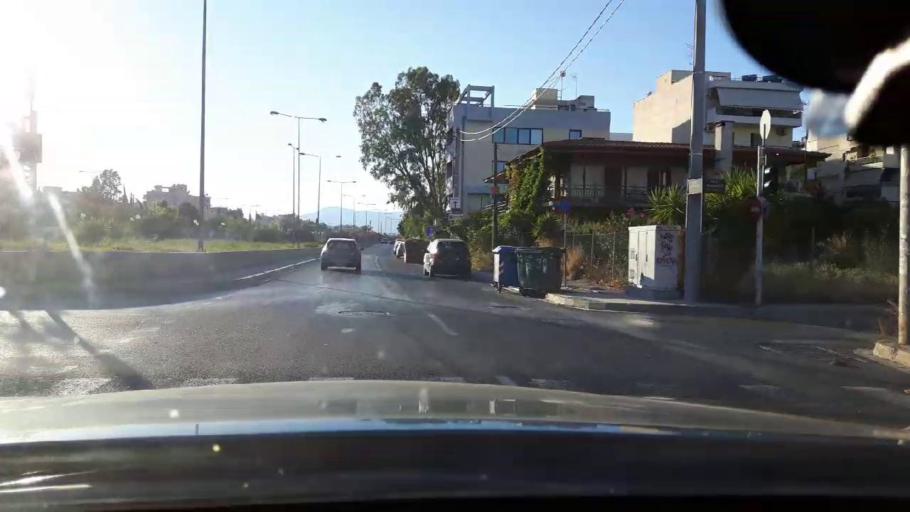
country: GR
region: Attica
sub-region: Nomarchia Athinas
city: Vrilissia
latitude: 38.0284
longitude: 23.8283
